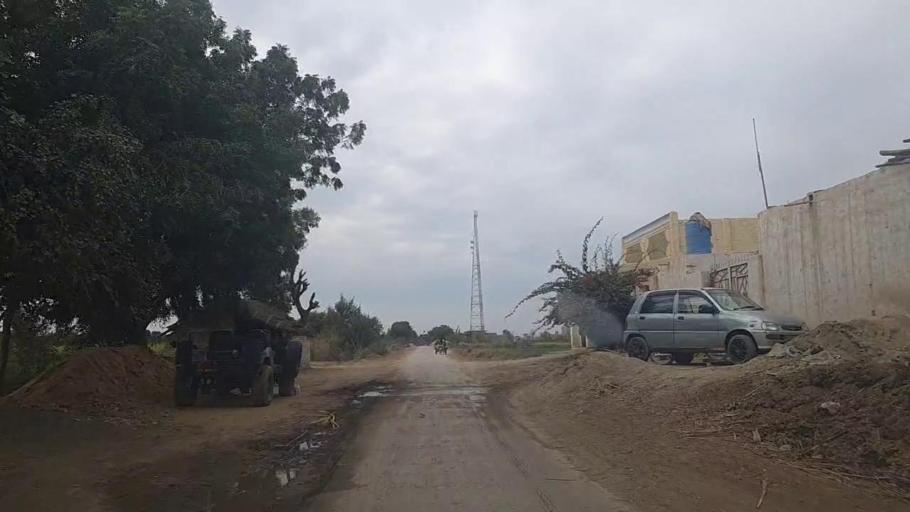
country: PK
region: Sindh
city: Khadro
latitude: 26.1288
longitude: 68.8057
